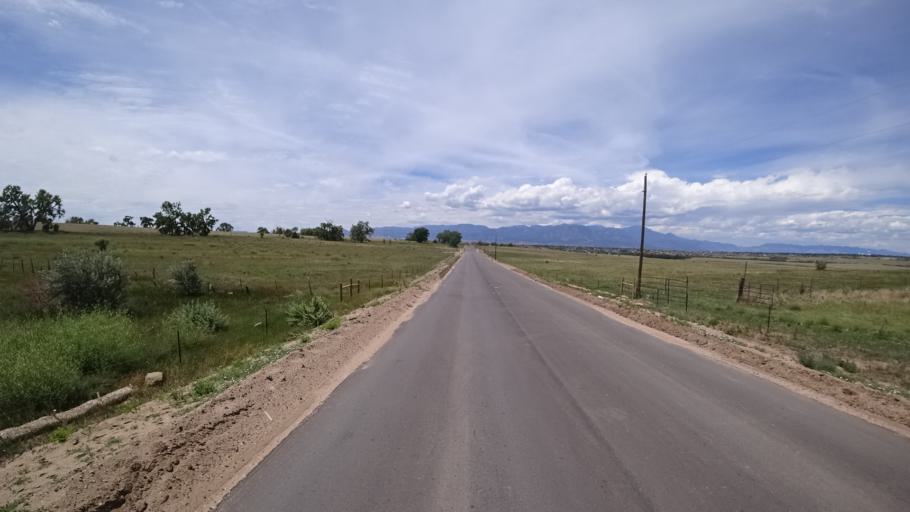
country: US
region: Colorado
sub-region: El Paso County
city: Fountain
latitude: 38.6940
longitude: -104.6550
